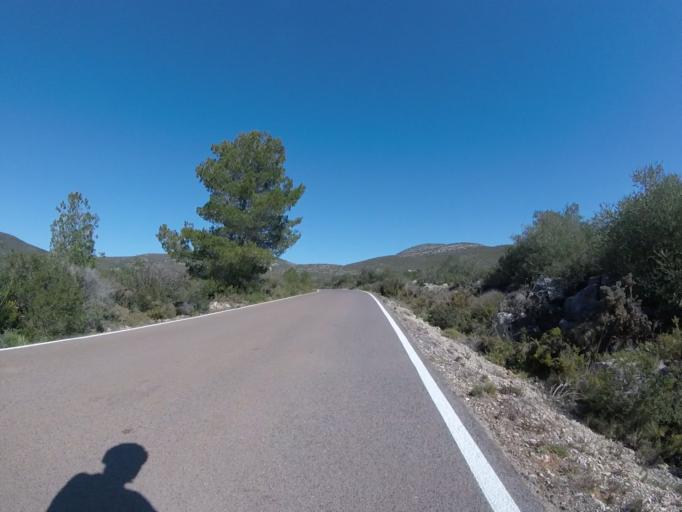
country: ES
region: Valencia
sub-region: Provincia de Castello
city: Santa Magdalena de Pulpis
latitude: 40.3757
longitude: 0.2717
